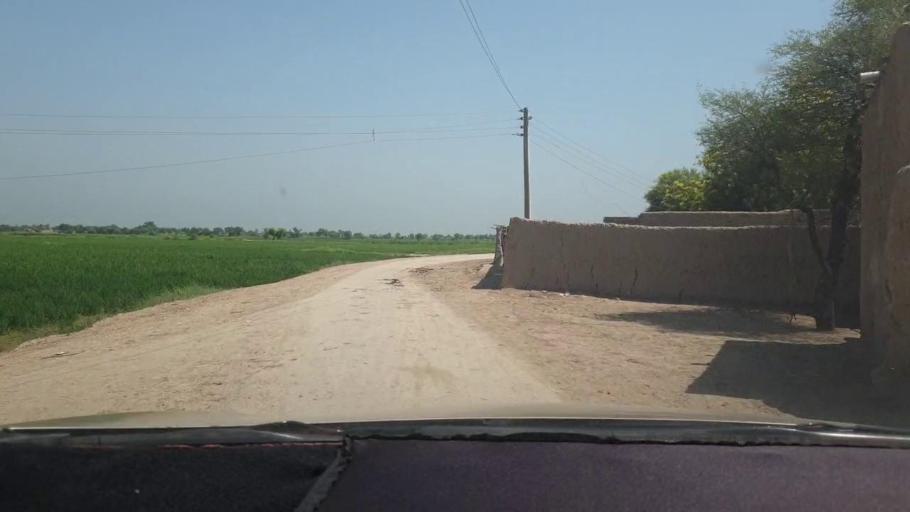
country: PK
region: Sindh
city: Miro Khan
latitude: 27.6698
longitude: 68.0988
